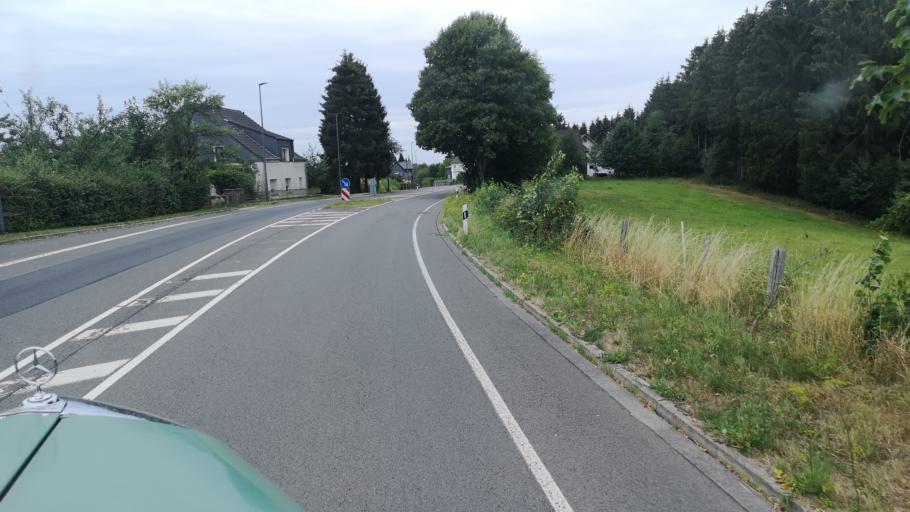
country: DE
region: North Rhine-Westphalia
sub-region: Regierungsbezirk Koln
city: Kurten
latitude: 51.0798
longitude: 7.3040
